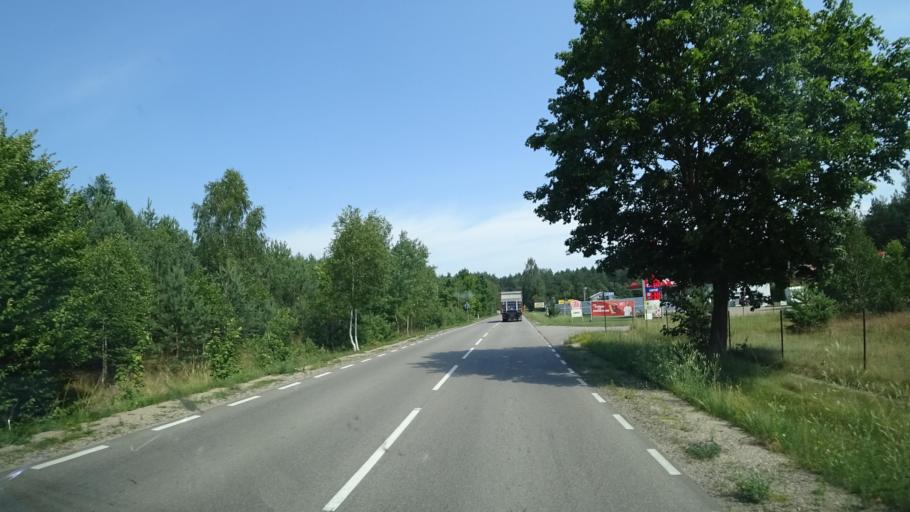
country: PL
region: Pomeranian Voivodeship
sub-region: Powiat koscierski
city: Lipusz
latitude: 54.0874
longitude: 17.7992
